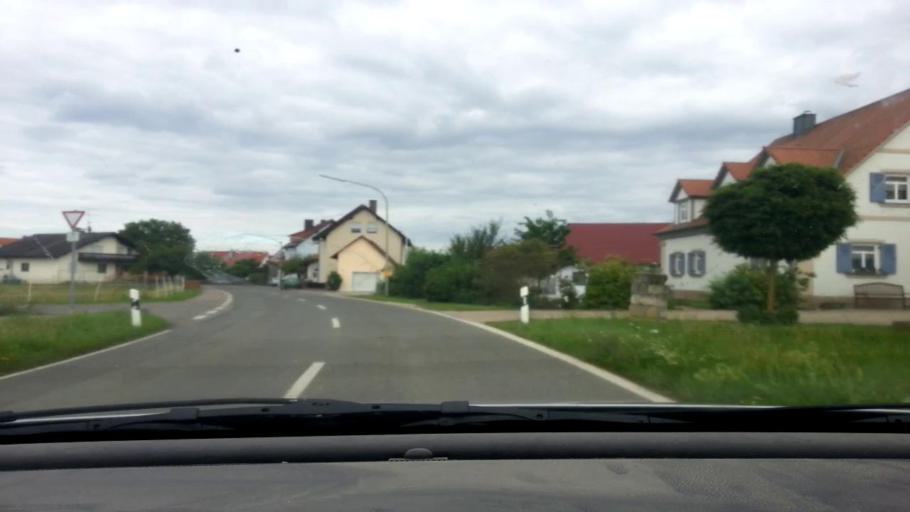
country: DE
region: Bavaria
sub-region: Upper Franconia
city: Gundelsheim
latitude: 49.9595
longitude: 10.9370
